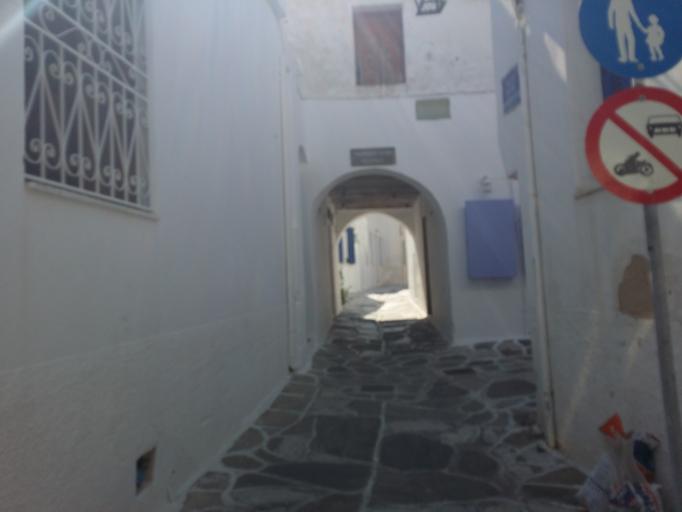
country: GR
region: South Aegean
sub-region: Nomos Kykladon
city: Paros
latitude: 37.0560
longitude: 25.2074
